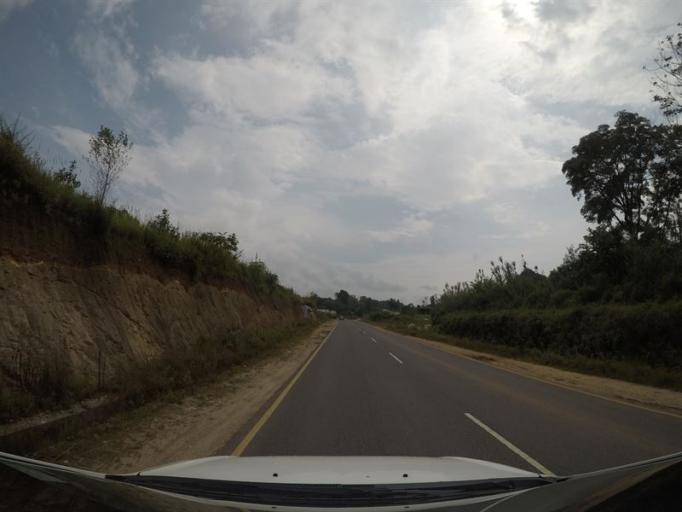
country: IN
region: Meghalaya
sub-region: East Khasi Hills
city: Shillong
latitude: 25.4862
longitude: 92.1918
